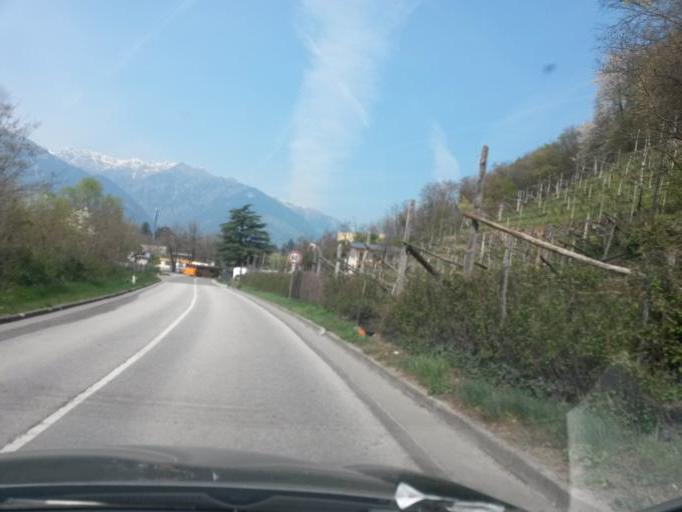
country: IT
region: Trentino-Alto Adige
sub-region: Bolzano
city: Sinigo
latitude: 46.6561
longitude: 11.1857
